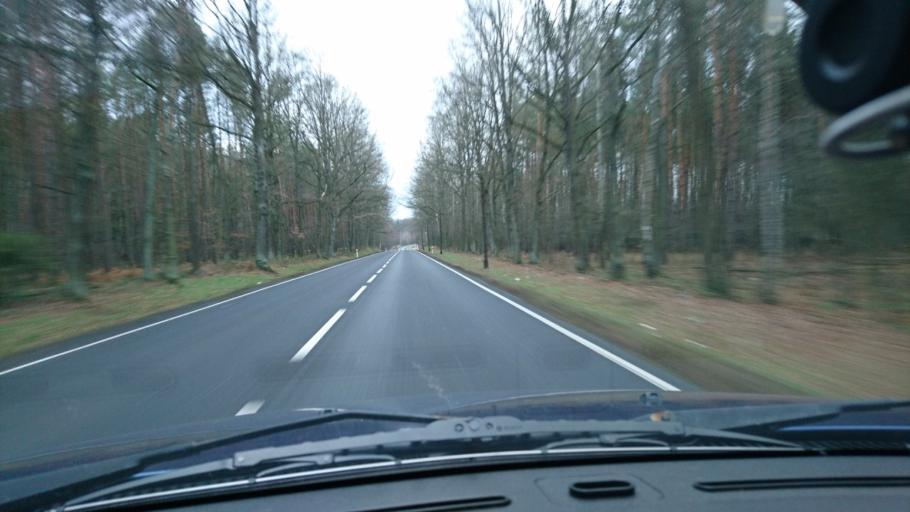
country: PL
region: Opole Voivodeship
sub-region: Powiat kluczborski
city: Kluczbork
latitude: 50.9503
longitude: 18.3128
